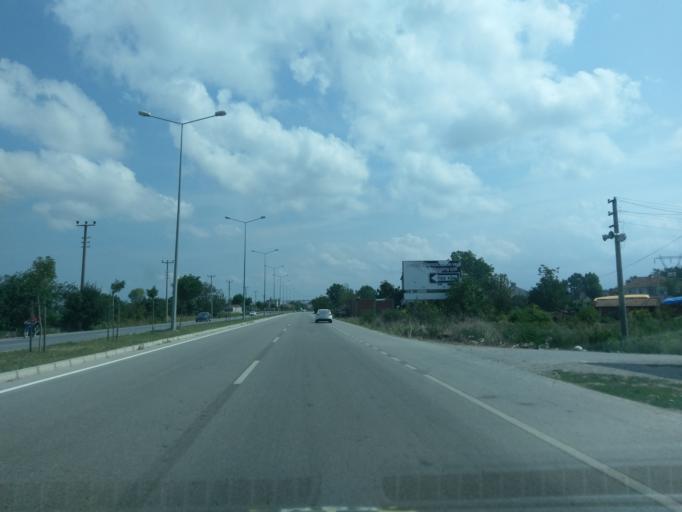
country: TR
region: Samsun
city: Bafra
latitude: 41.5732
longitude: 35.8672
